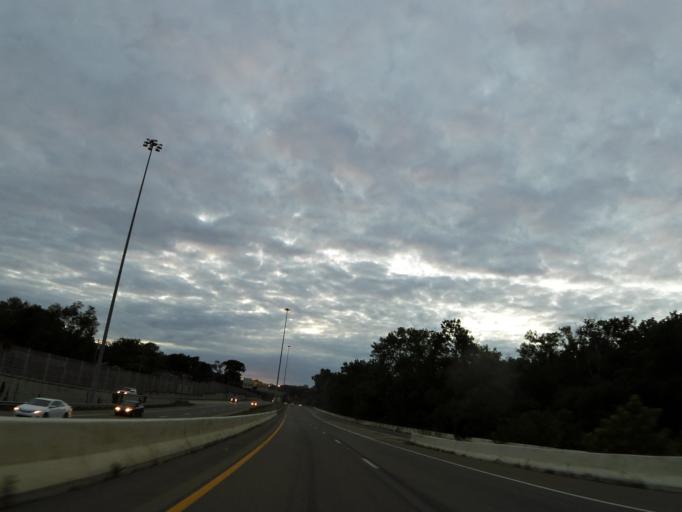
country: US
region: Tennessee
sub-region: Davidson County
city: Belle Meade
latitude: 36.1572
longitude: -86.8597
